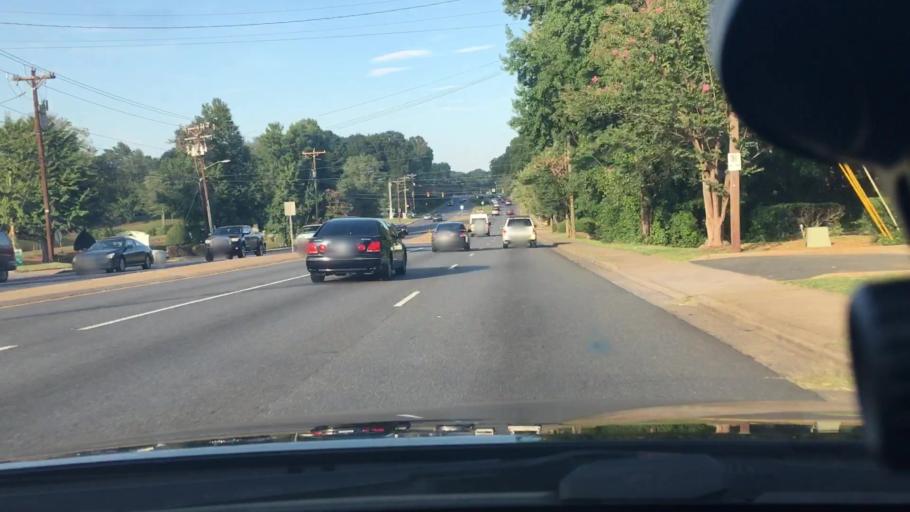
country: US
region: North Carolina
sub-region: Mecklenburg County
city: Mint Hill
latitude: 35.2042
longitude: -80.7204
